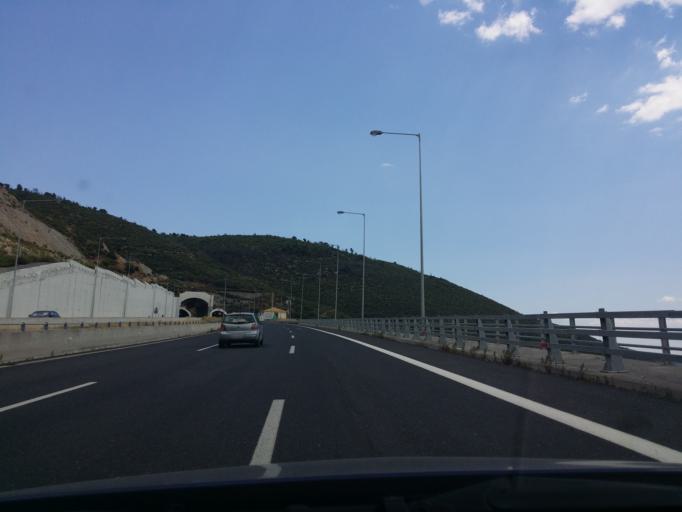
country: GR
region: Peloponnese
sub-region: Nomos Arkadias
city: Megalopoli
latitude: 37.3865
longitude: 22.1926
